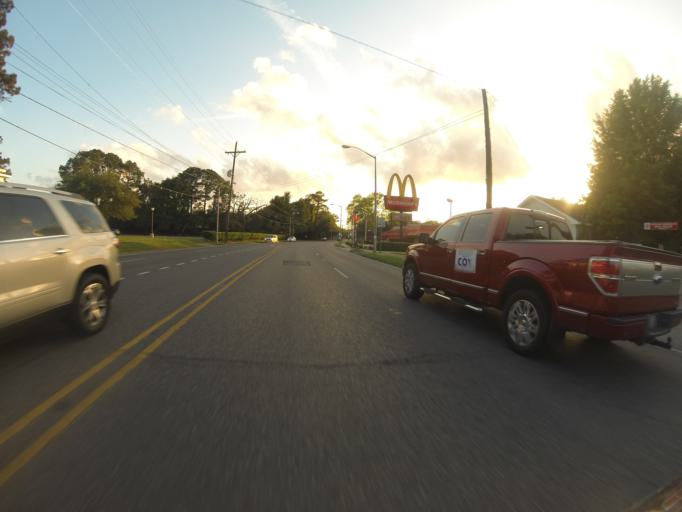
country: US
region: Louisiana
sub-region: Lafayette Parish
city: Lafayette
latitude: 30.2147
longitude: -92.0216
